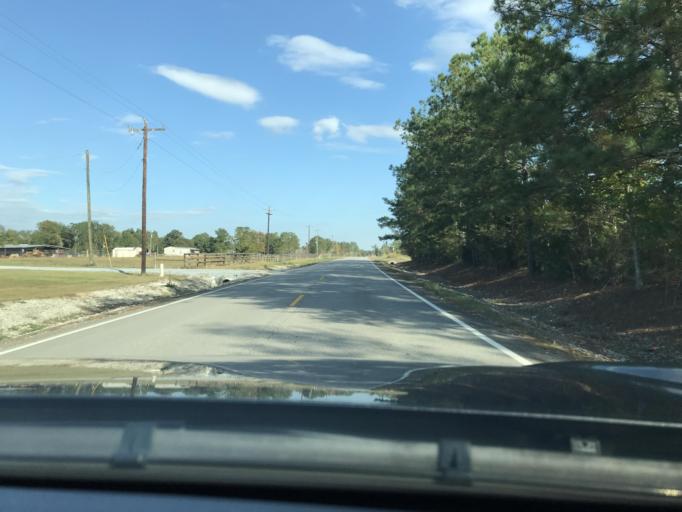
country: US
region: Louisiana
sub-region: Calcasieu Parish
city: Moss Bluff
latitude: 30.3394
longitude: -93.2540
